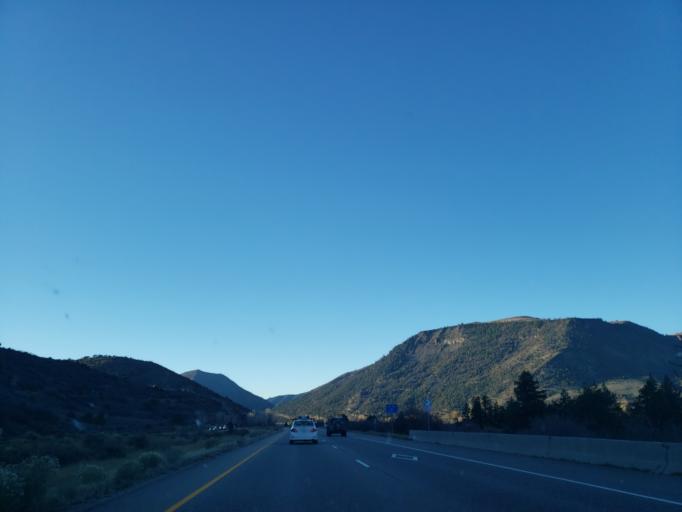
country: US
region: Colorado
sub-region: Pitkin County
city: Snowmass Village
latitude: 39.2795
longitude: -106.8978
